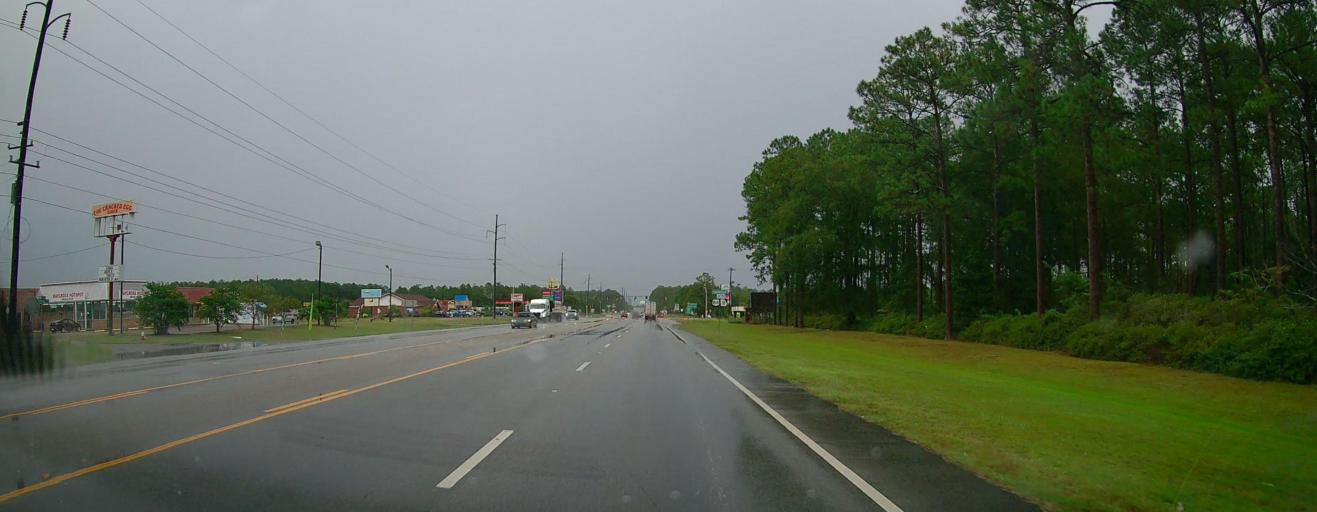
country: US
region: Georgia
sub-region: Ware County
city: Deenwood
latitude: 31.2087
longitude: -82.3868
